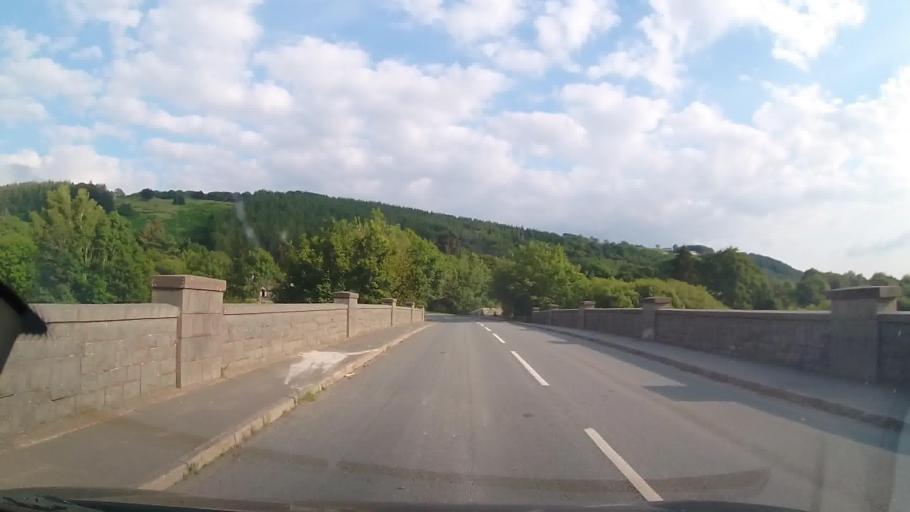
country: GB
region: Wales
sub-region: Gwynedd
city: Bala
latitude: 52.9033
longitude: -3.5929
